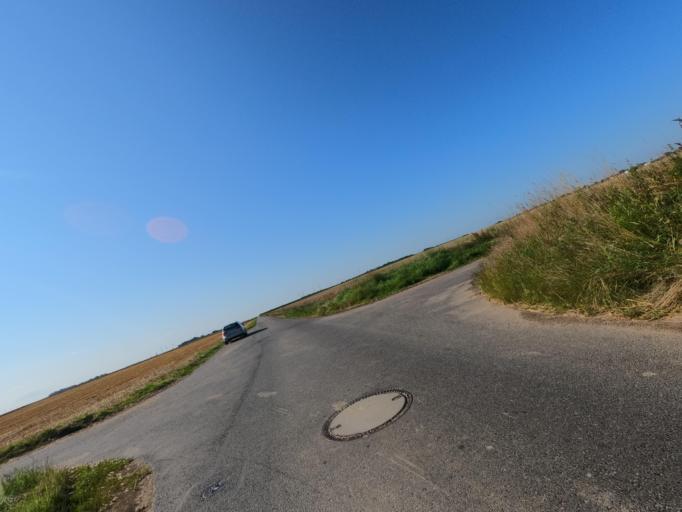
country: DE
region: North Rhine-Westphalia
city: Erkelenz
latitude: 51.0742
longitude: 6.3680
